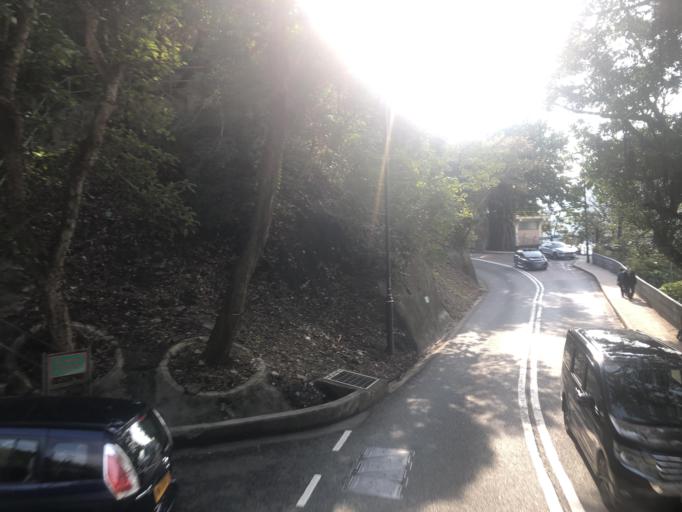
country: HK
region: Wanchai
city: Wan Chai
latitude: 22.2421
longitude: 114.1882
